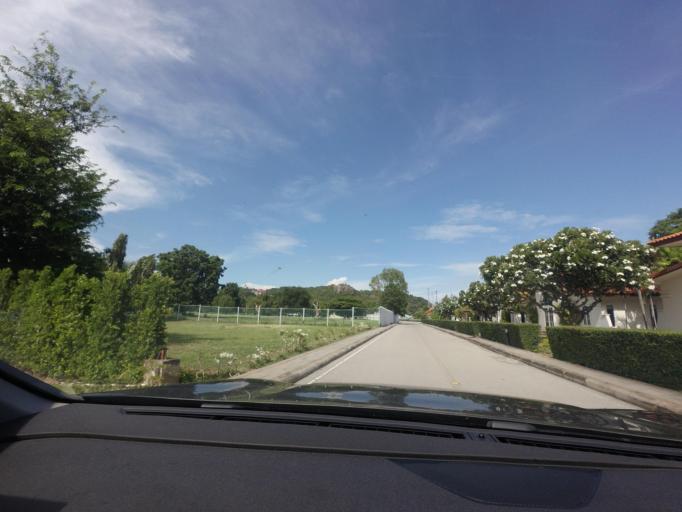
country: TH
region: Prachuap Khiri Khan
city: Hua Hin
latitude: 12.5163
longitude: 99.9606
